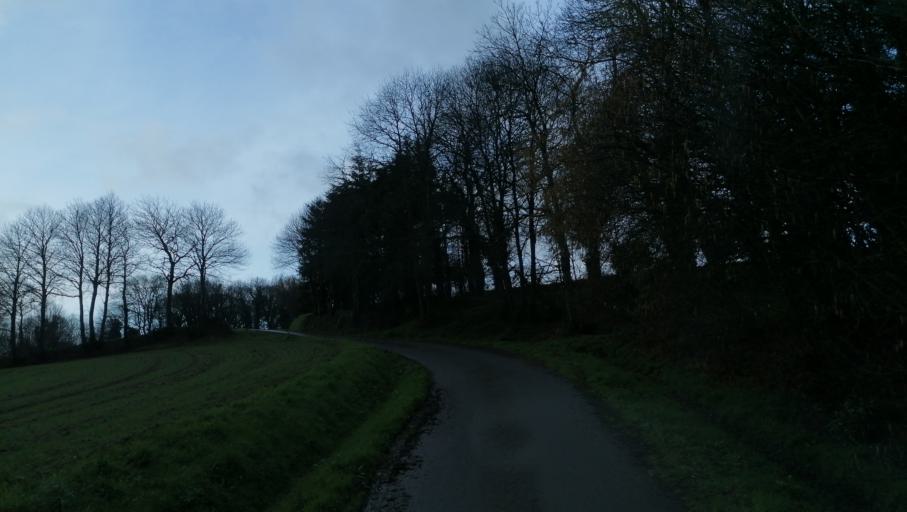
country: FR
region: Brittany
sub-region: Departement des Cotes-d'Armor
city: Plouagat
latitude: 48.4971
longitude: -2.9718
